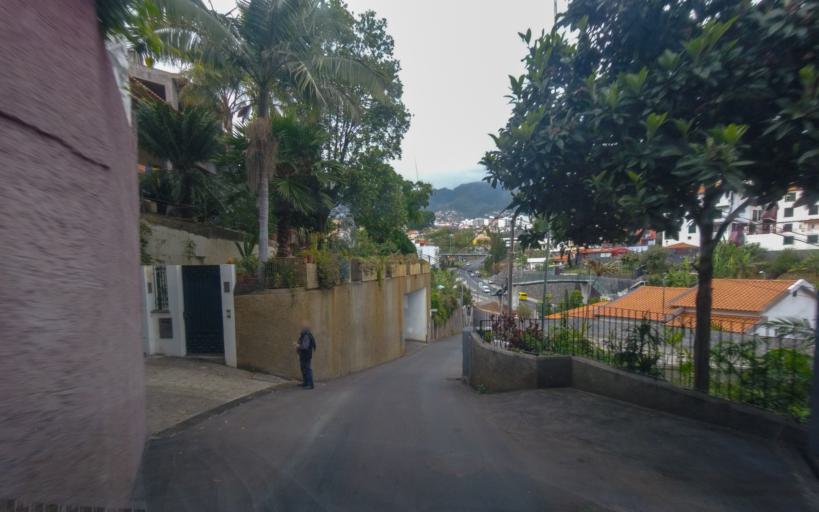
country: PT
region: Madeira
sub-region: Funchal
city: Funchal
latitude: 32.6483
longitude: -16.9268
